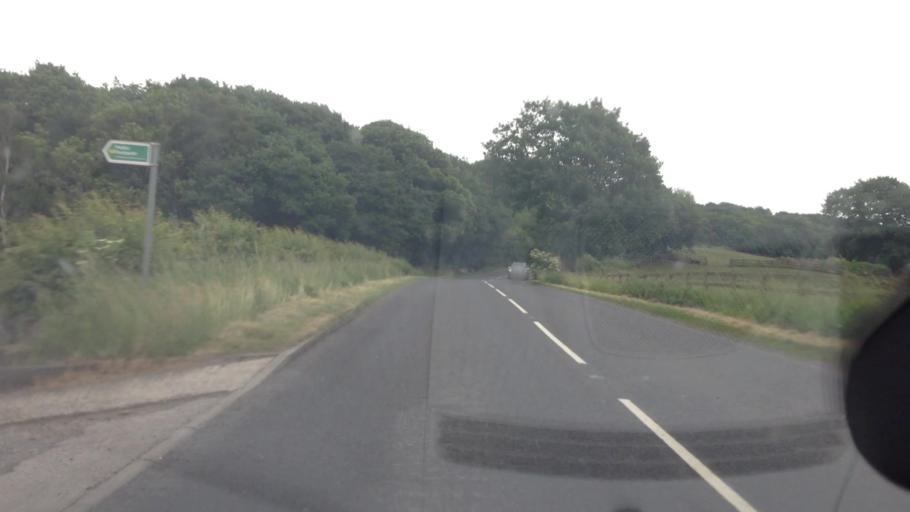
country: GB
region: England
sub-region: City and Borough of Wakefield
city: Crigglestone
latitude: 53.6193
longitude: -1.5452
